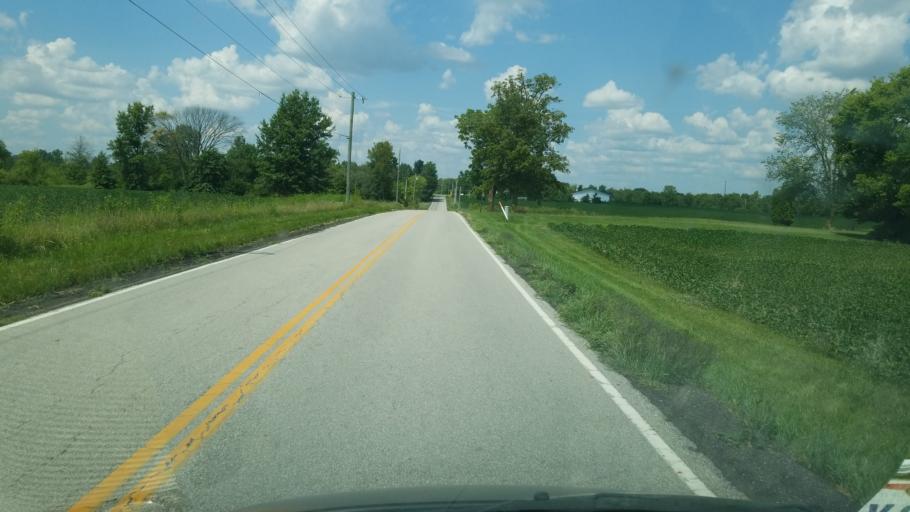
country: US
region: Ohio
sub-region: Champaign County
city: North Lewisburg
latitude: 40.3263
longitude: -83.4733
